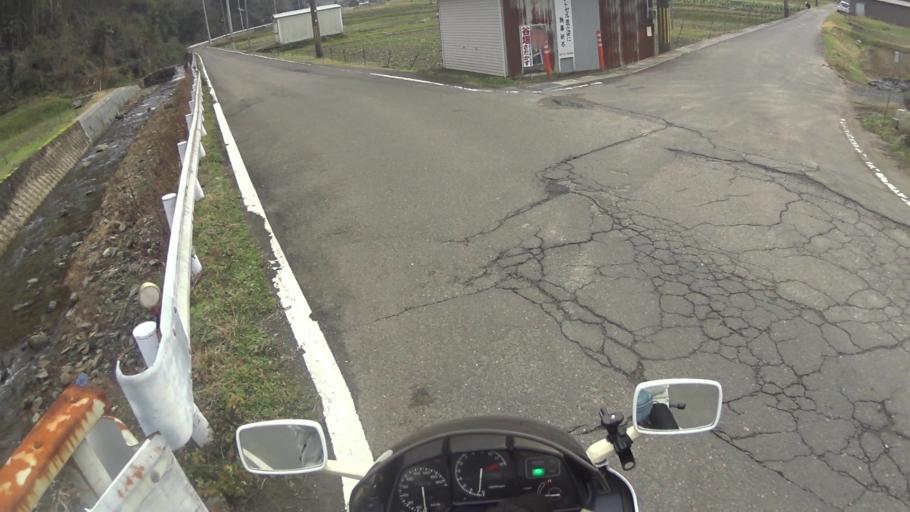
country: JP
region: Kyoto
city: Maizuru
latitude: 35.4257
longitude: 135.2979
